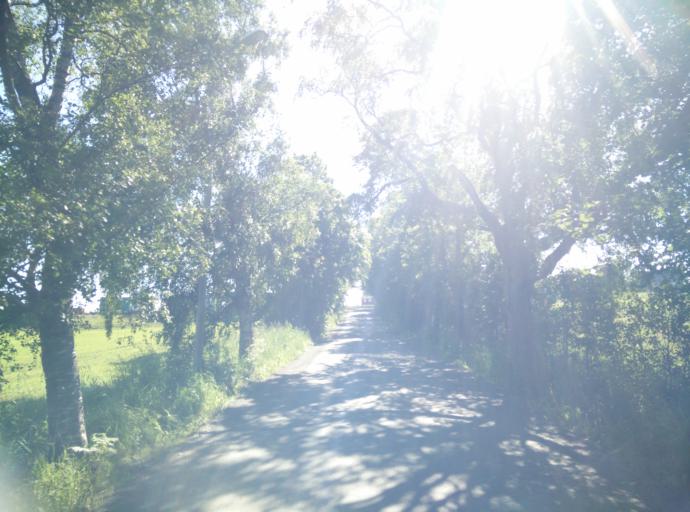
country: NO
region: Sor-Trondelag
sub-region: Trondheim
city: Trondheim
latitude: 63.4080
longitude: 10.3725
